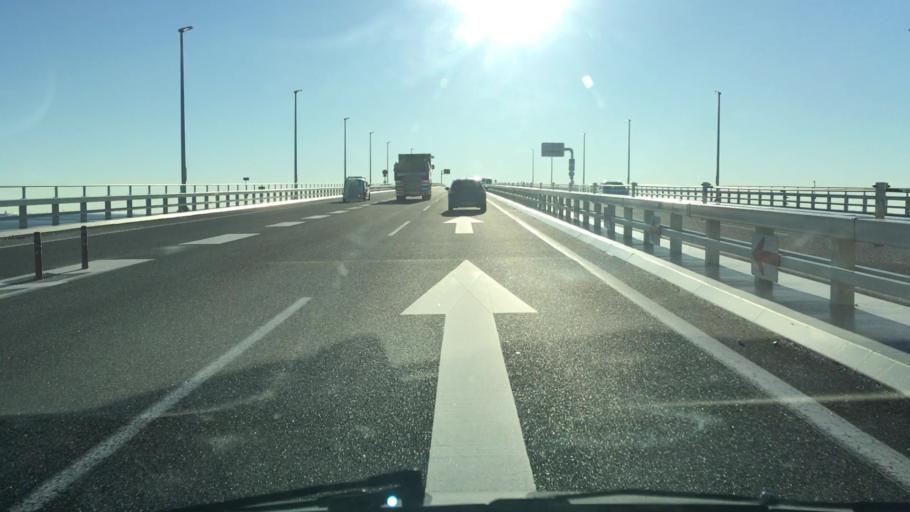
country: JP
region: Chiba
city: Kisarazu
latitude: 35.4603
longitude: 139.8805
